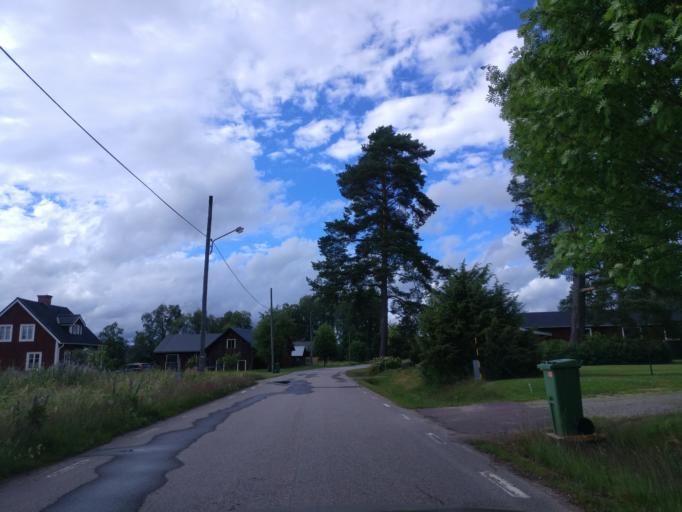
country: SE
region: Vaermland
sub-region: Munkfors Kommun
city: Munkfors
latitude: 59.9695
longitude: 13.4876
